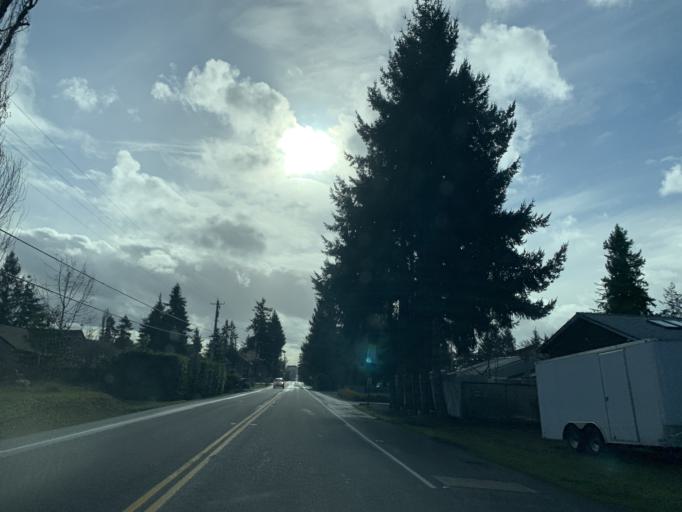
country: US
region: Washington
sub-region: King County
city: Lakeland South
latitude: 47.2731
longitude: -122.2978
